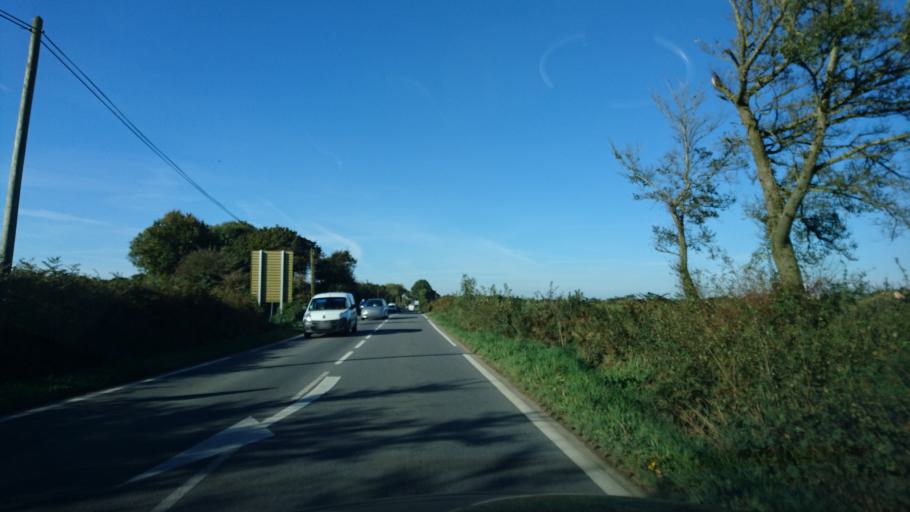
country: FR
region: Brittany
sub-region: Departement du Finistere
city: Bohars
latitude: 48.4496
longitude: -4.5369
